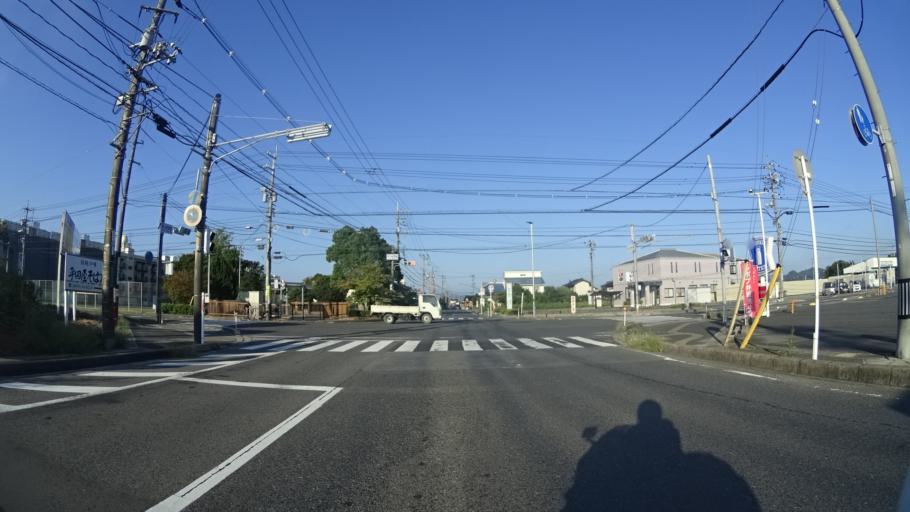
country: JP
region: Shimane
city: Sakaiminato
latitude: 35.5188
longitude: 133.2152
